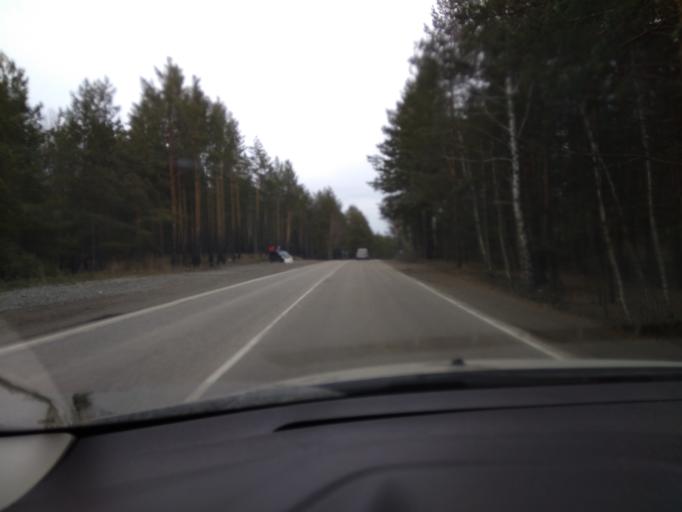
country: RU
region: Chelyabinsk
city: Kyshtym
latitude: 55.7086
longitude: 60.5905
